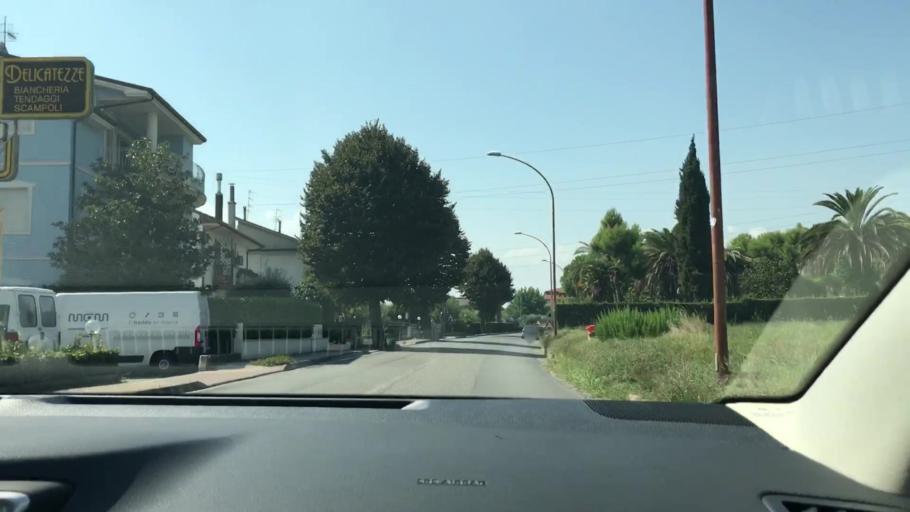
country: IT
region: The Marches
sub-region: Provincia di Ascoli Piceno
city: San Benedetto del Tronto
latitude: 42.9068
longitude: 13.8728
